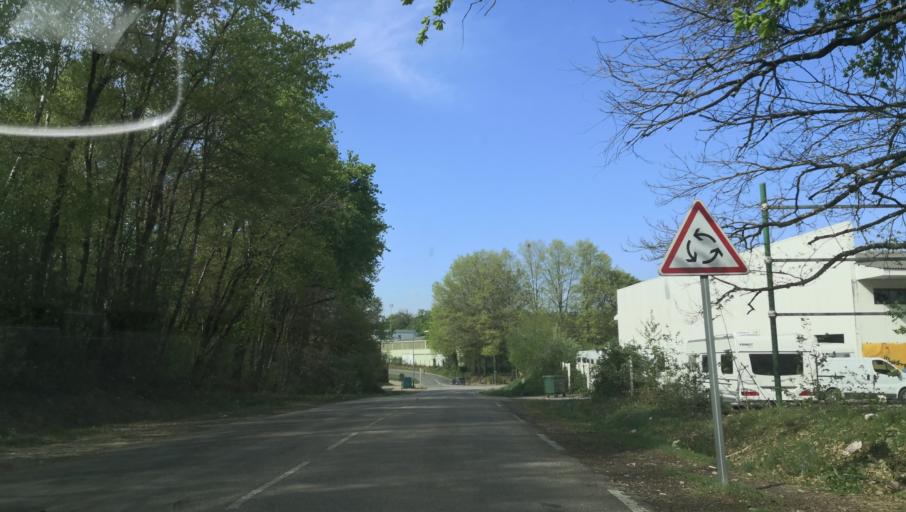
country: FR
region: Limousin
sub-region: Departement de la Haute-Vienne
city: Couzeix
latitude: 45.8675
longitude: 1.2592
